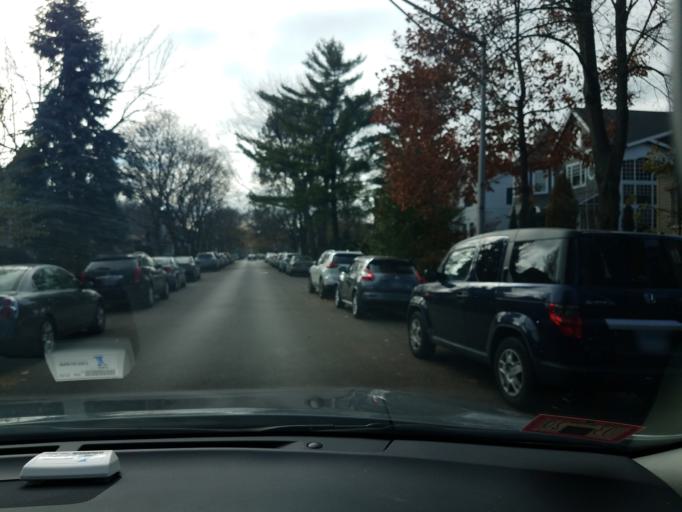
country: US
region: Illinois
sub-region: Cook County
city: Lincolnwood
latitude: 41.9510
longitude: -87.7339
